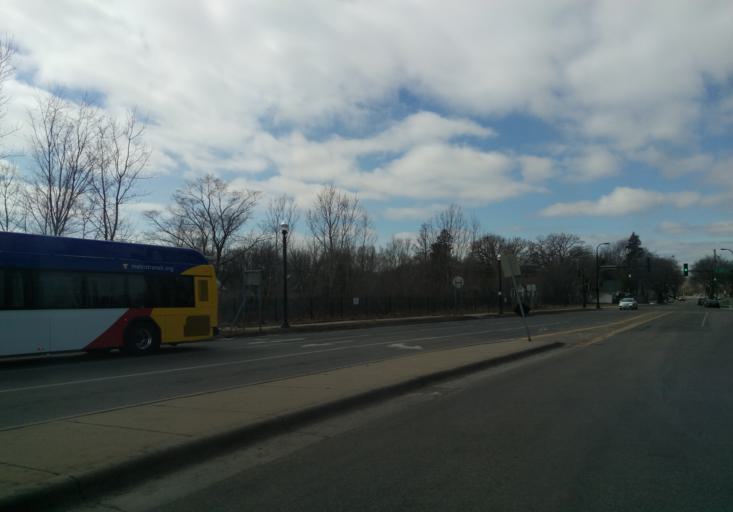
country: US
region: Minnesota
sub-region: Hennepin County
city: Richfield
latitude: 44.9198
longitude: -93.2193
